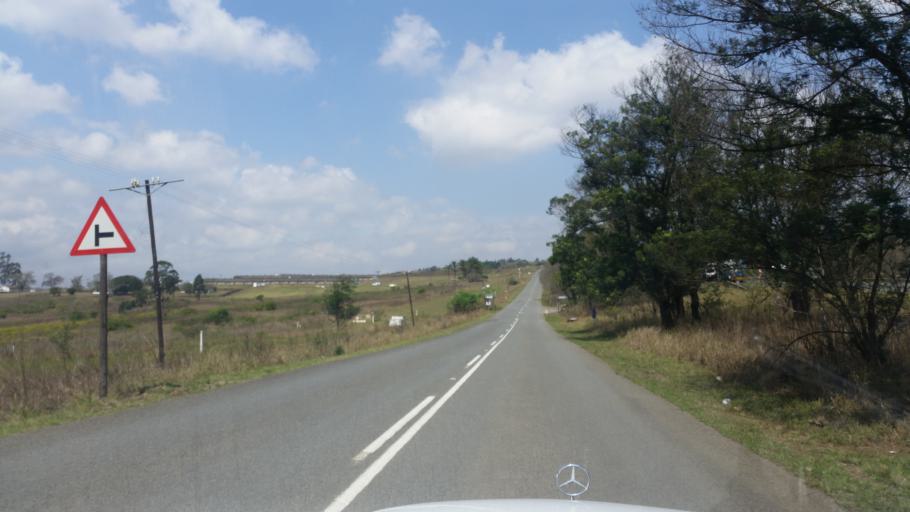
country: ZA
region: KwaZulu-Natal
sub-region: uMgungundlovu District Municipality
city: Camperdown
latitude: -29.7015
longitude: 30.4917
